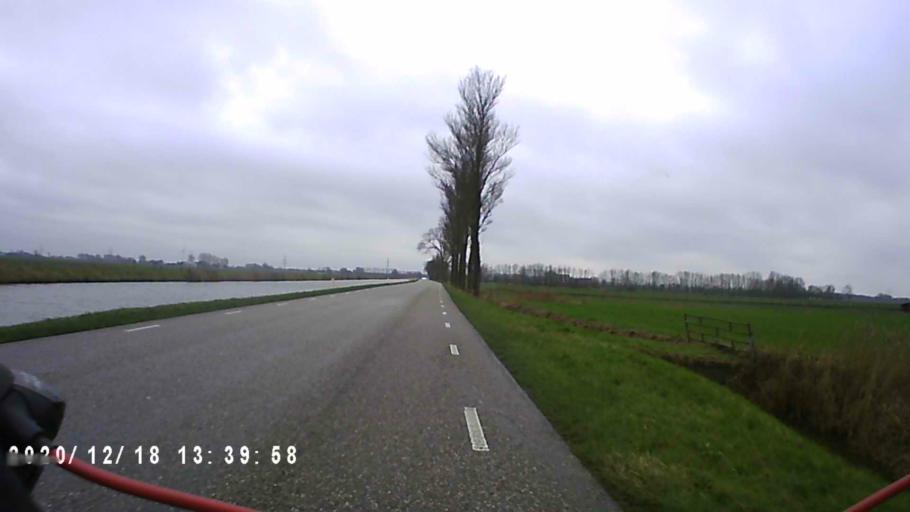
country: NL
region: Groningen
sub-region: Gemeente Bedum
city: Bedum
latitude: 53.3254
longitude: 6.5941
